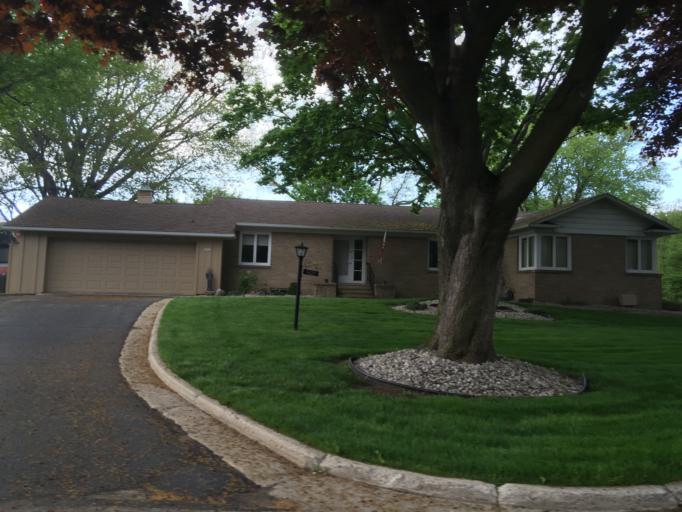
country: US
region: Michigan
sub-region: Menominee County
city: Menominee
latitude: 45.1169
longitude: -87.6130
